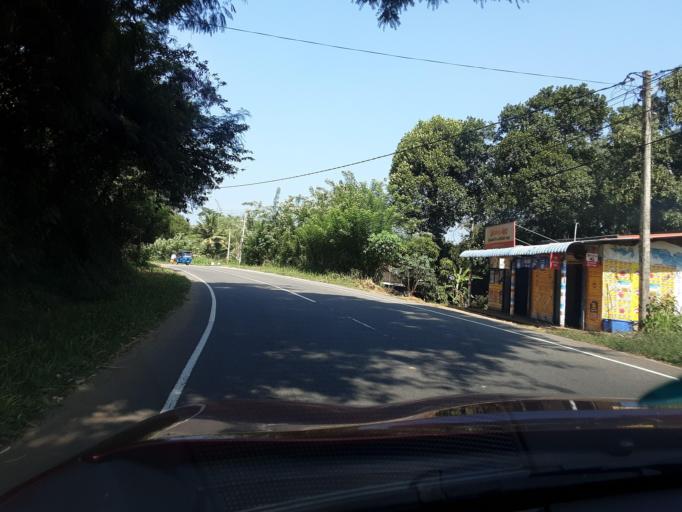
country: LK
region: Uva
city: Badulla
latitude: 7.1813
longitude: 81.0476
